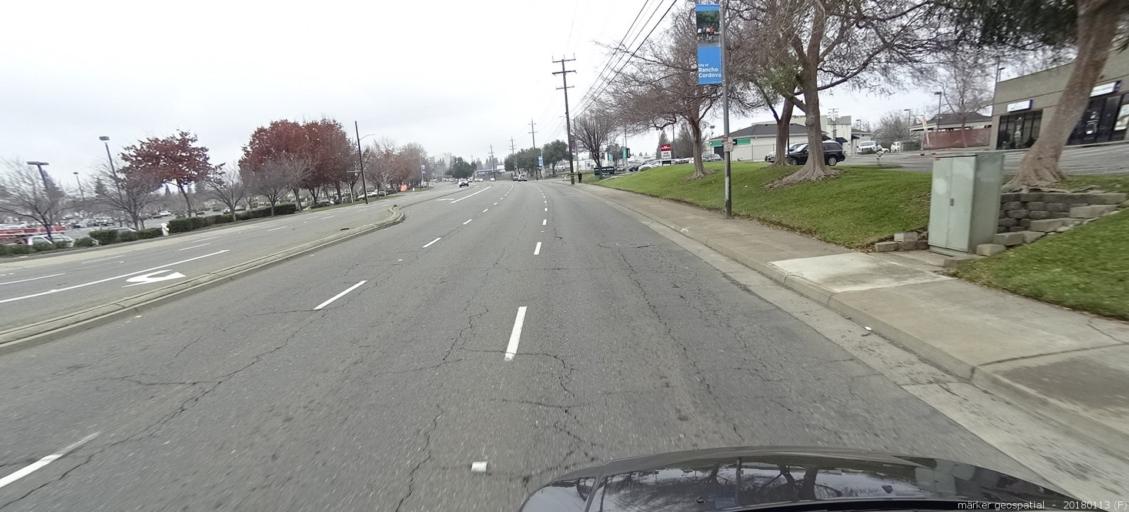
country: US
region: California
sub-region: Sacramento County
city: Gold River
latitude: 38.6001
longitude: -121.2658
